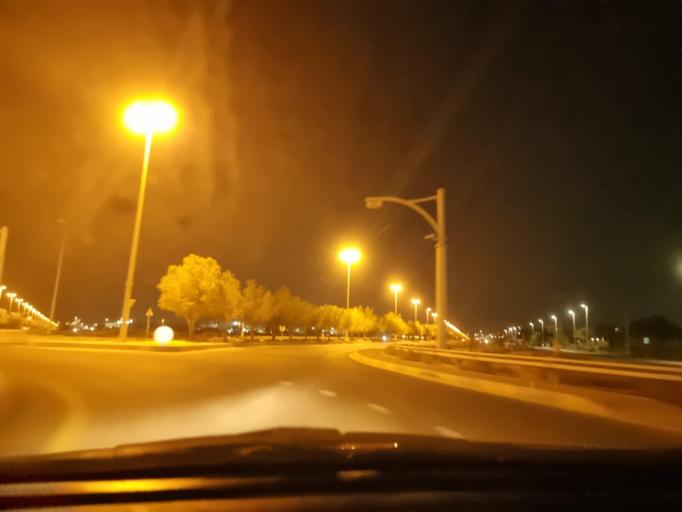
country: AE
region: Abu Dhabi
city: Abu Dhabi
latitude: 24.3745
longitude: 54.6974
